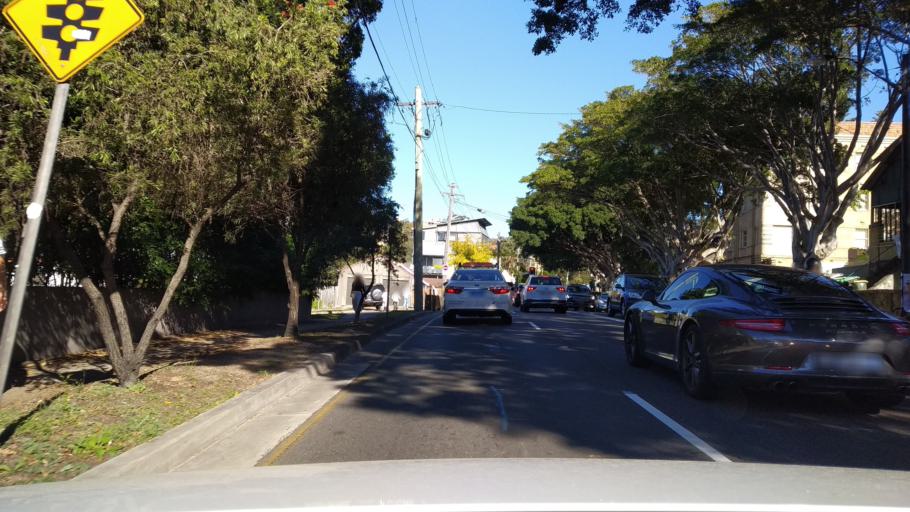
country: AU
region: New South Wales
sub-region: Waverley
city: Bondi Beach
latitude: -33.8869
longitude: 151.2661
